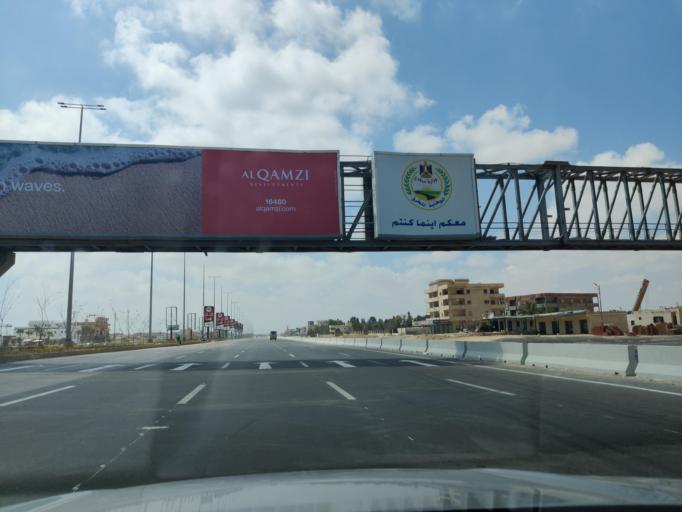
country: EG
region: Muhafazat Matruh
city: Al `Alamayn
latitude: 30.9476
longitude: 28.7753
